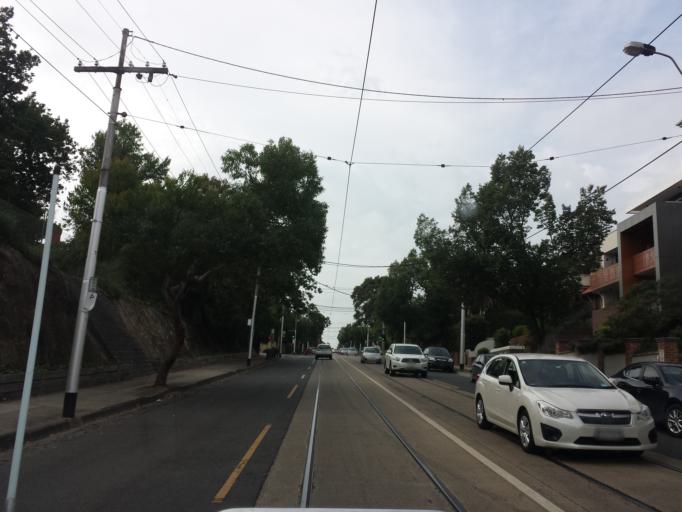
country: AU
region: Victoria
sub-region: Boroondara
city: Hawthorn East
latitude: -37.8342
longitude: 145.0332
